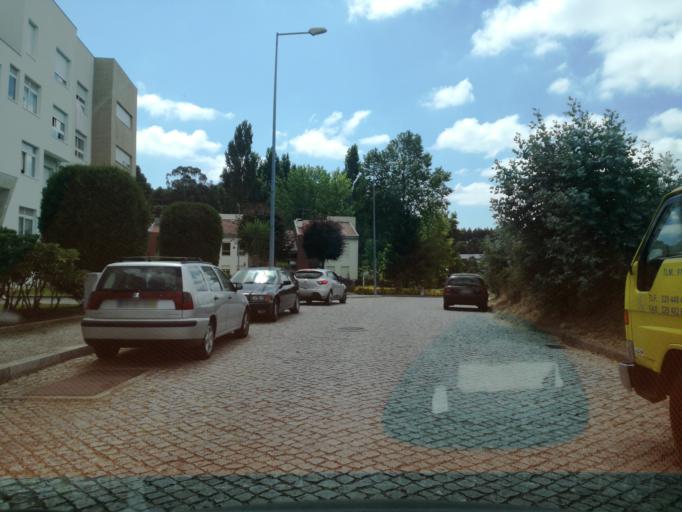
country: PT
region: Porto
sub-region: Maia
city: Nogueira
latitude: 41.2451
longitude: -8.5973
